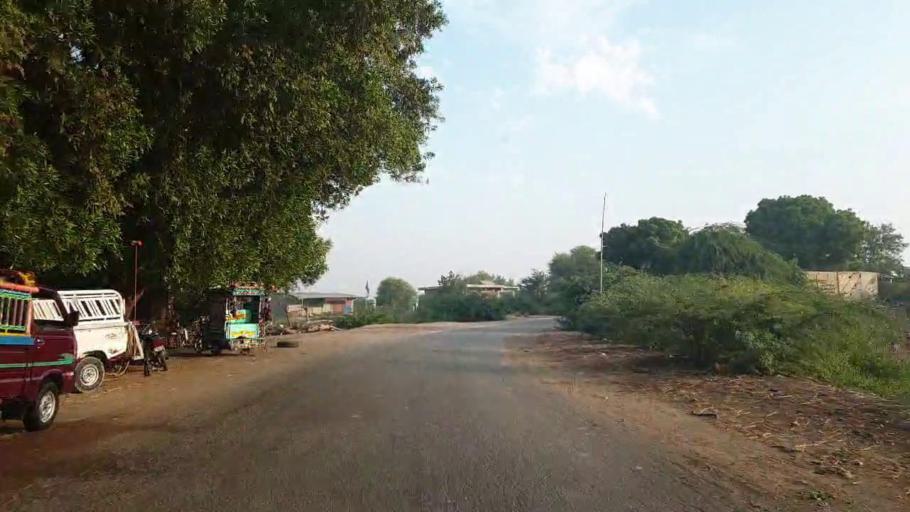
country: PK
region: Sindh
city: Tando Bago
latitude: 24.7192
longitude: 68.9401
